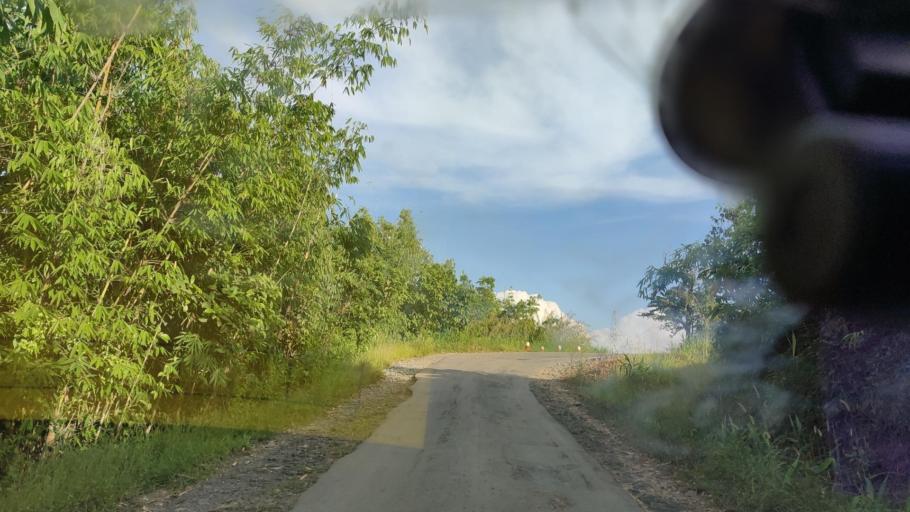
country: MM
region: Magway
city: Minbu
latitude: 19.8689
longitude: 94.1760
